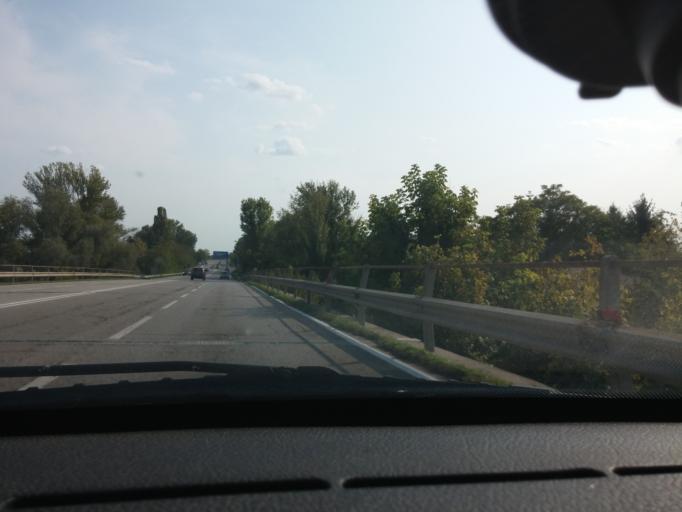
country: IT
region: Emilia-Romagna
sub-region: Provincia di Ferrara
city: Gaibanella-Sant'Edigio
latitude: 44.8009
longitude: 11.6366
